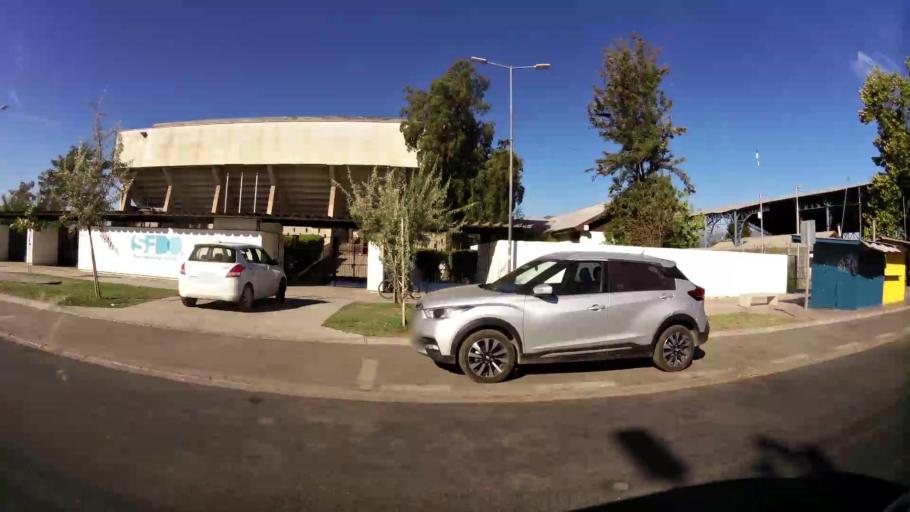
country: CL
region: O'Higgins
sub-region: Provincia de Colchagua
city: Chimbarongo
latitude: -34.5793
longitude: -70.9876
